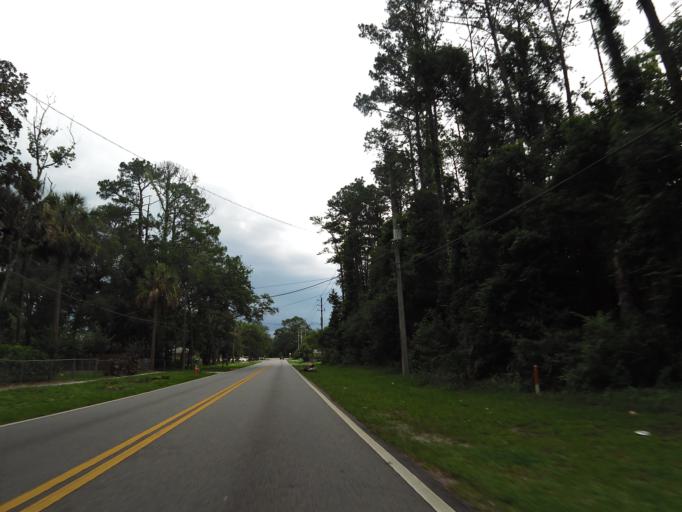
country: US
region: Florida
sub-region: Duval County
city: Jacksonville
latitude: 30.2827
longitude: -81.5820
